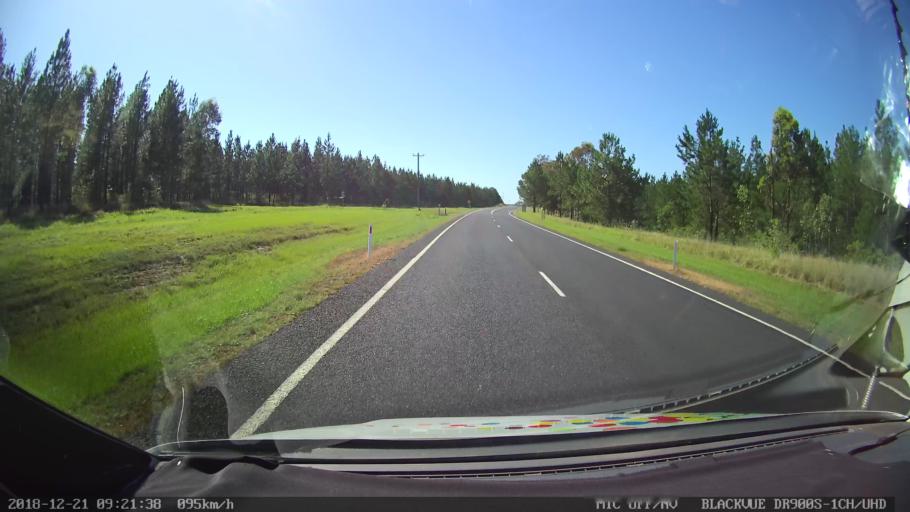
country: AU
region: New South Wales
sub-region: Clarence Valley
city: Maclean
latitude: -29.3318
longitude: 152.9991
